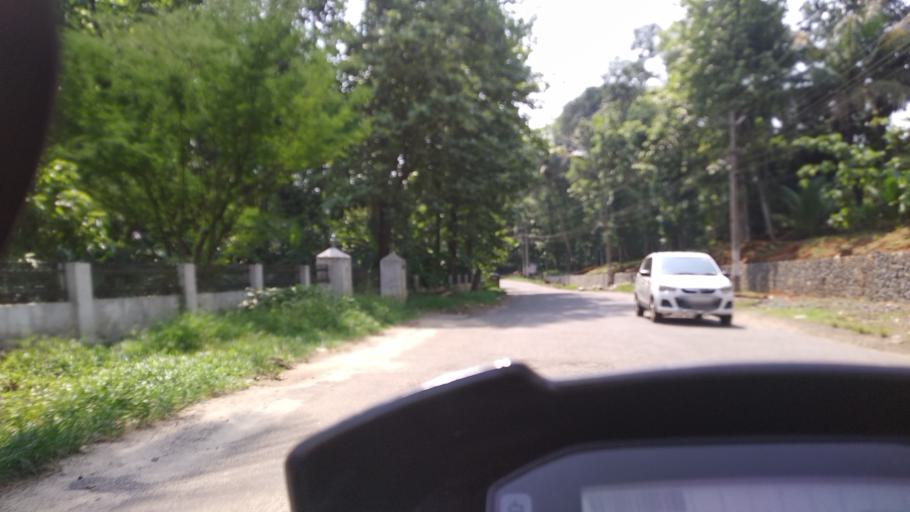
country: IN
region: Kerala
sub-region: Kottayam
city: Erattupetta
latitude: 9.6974
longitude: 76.8047
